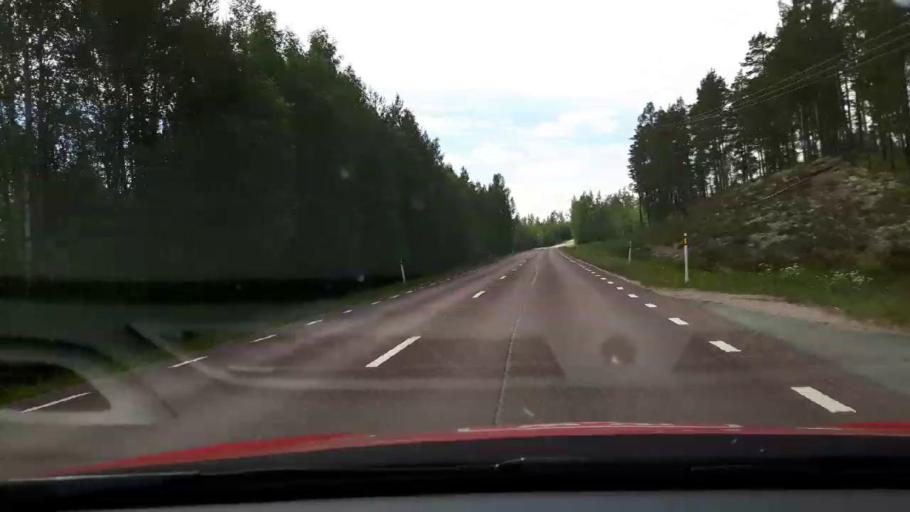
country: SE
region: Jaemtland
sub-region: Harjedalens Kommun
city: Sveg
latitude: 62.0543
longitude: 14.9020
